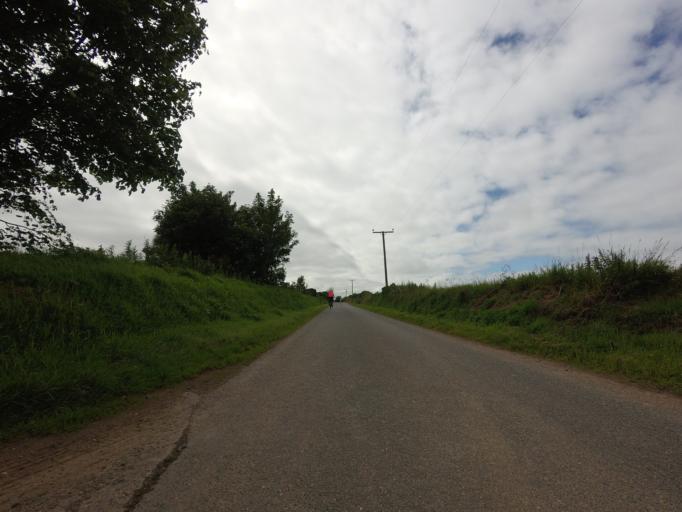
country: GB
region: Scotland
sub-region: Aberdeenshire
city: Turriff
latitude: 57.5449
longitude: -2.2824
